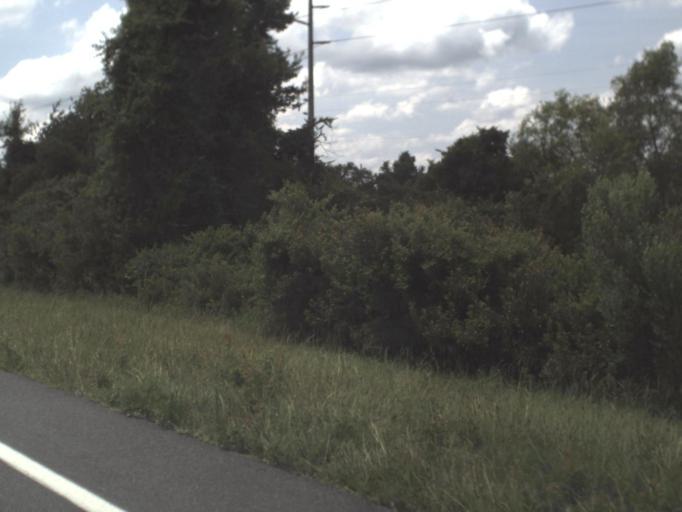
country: US
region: Florida
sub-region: Hamilton County
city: Jasper
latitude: 30.4461
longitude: -82.8820
